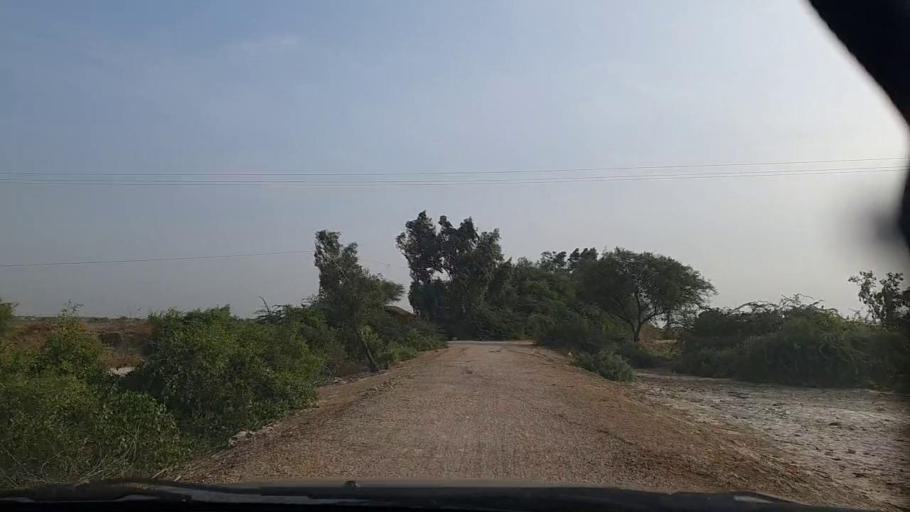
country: PK
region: Sindh
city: Thatta
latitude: 24.7316
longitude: 67.9152
